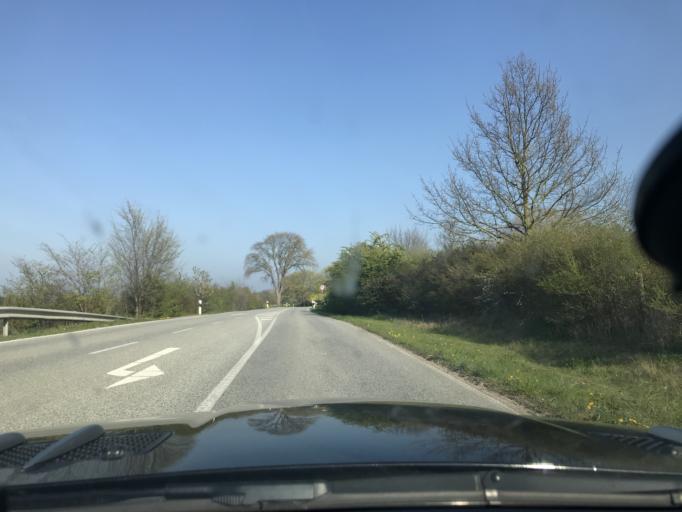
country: DE
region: Schleswig-Holstein
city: Heiligenhafen
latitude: 54.3654
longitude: 11.0145
